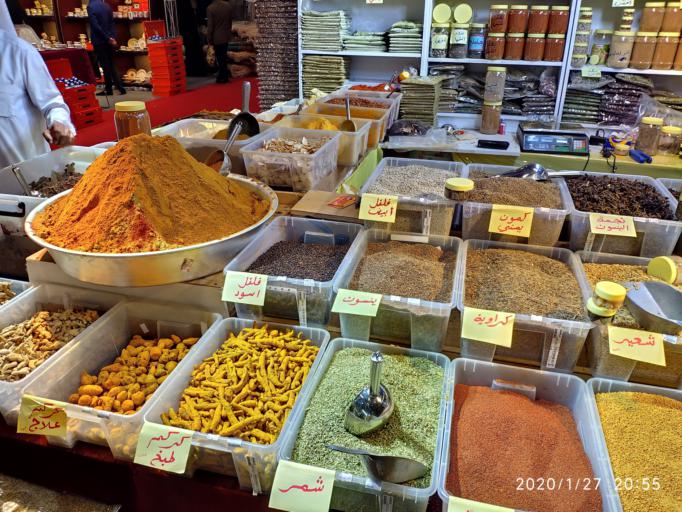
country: QA
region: Baladiyat ad Dawhah
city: Doha
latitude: 25.3228
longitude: 51.5317
